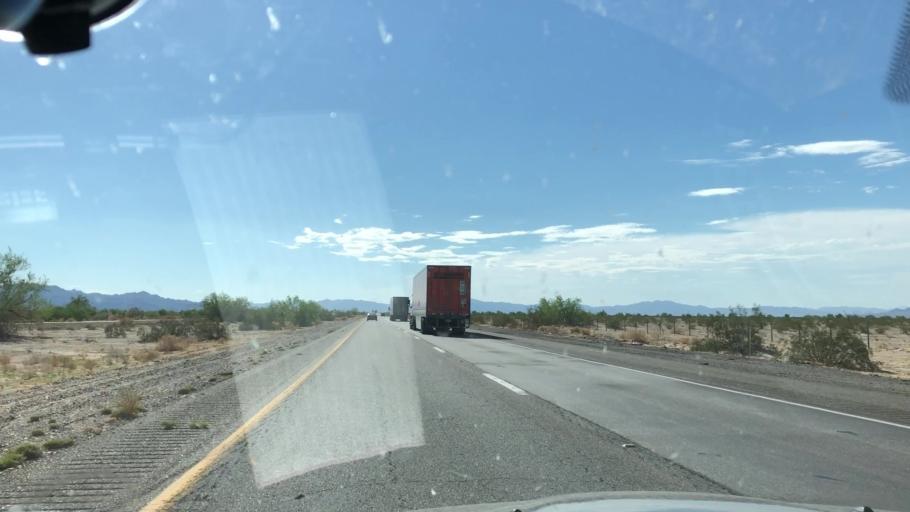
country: US
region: California
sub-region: Riverside County
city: Mesa Verde
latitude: 33.6587
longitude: -115.1625
